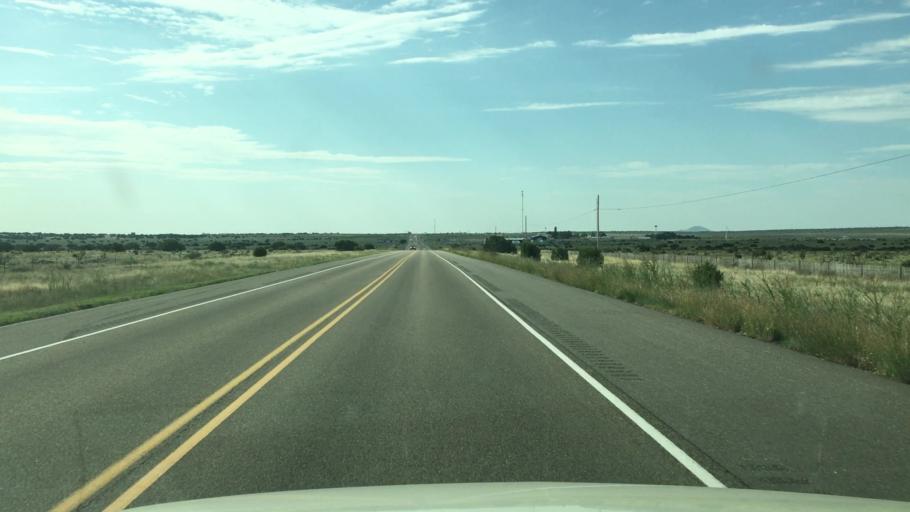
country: US
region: New Mexico
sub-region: Torrance County
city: Moriarty
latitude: 35.0255
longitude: -105.6739
